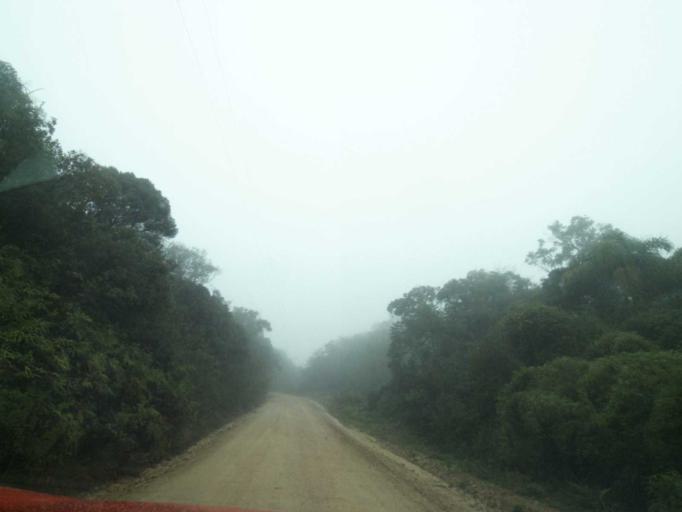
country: BR
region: Santa Catarina
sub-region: Anitapolis
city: Anitapolis
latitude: -27.9072
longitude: -49.1668
